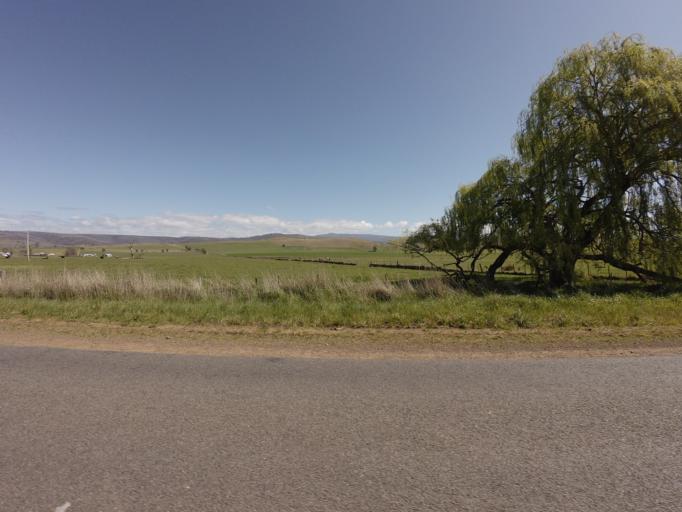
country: AU
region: Tasmania
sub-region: Derwent Valley
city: New Norfolk
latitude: -42.5562
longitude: 146.8065
